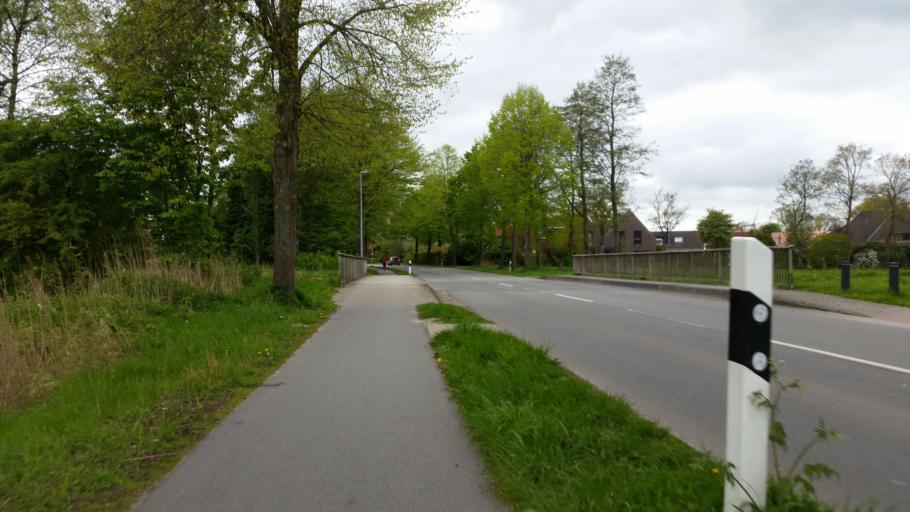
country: DE
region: Lower Saxony
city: Aurich
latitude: 53.4777
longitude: 7.4565
